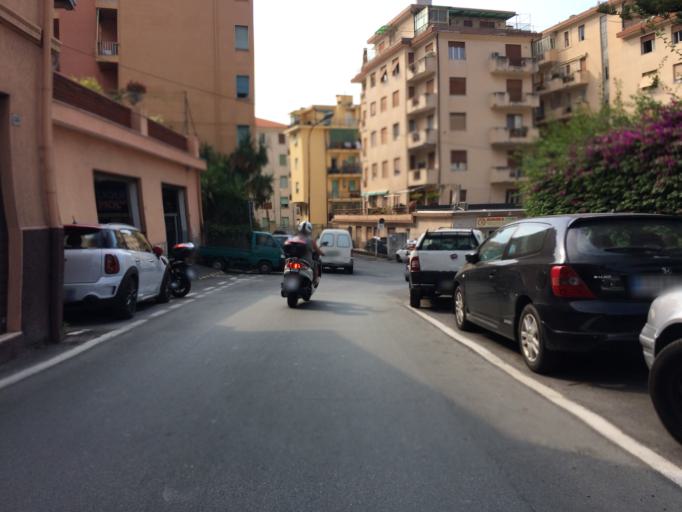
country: IT
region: Liguria
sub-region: Provincia di Imperia
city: San Remo
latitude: 43.8220
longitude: 7.7767
